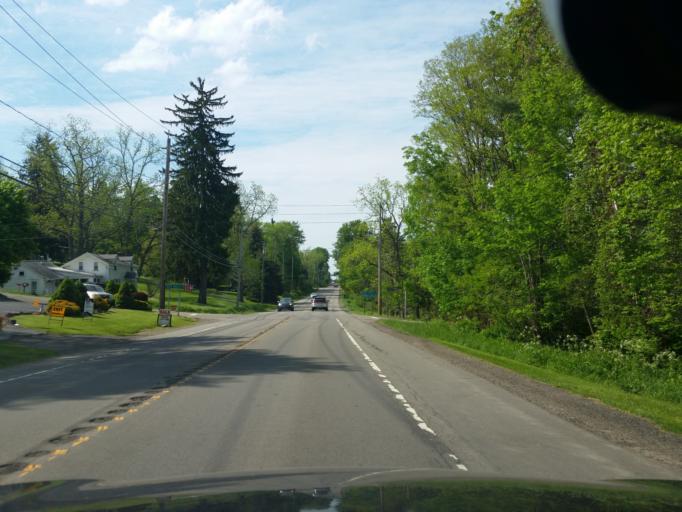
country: US
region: New York
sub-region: Chautauqua County
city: Lakewood
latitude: 42.1175
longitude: -79.3890
